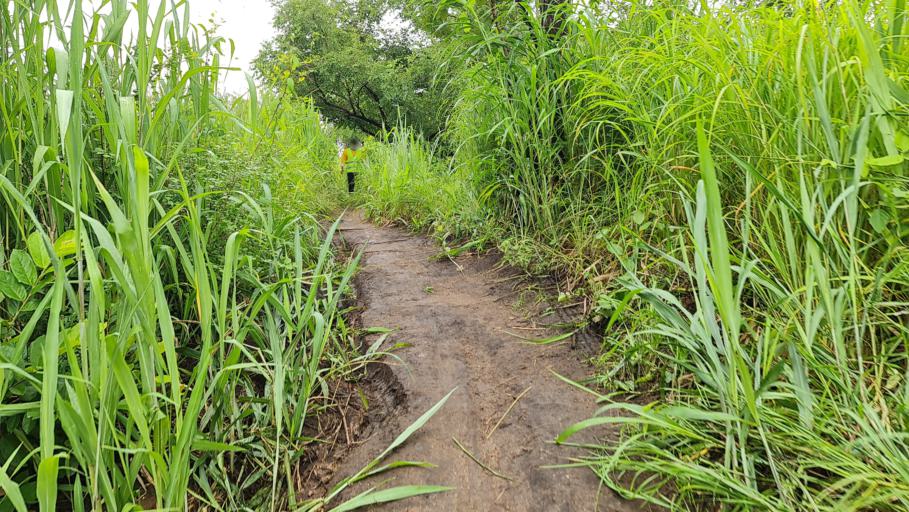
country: MW
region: Southern Region
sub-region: Nsanje District
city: Nsanje
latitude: -17.3967
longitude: 35.7893
